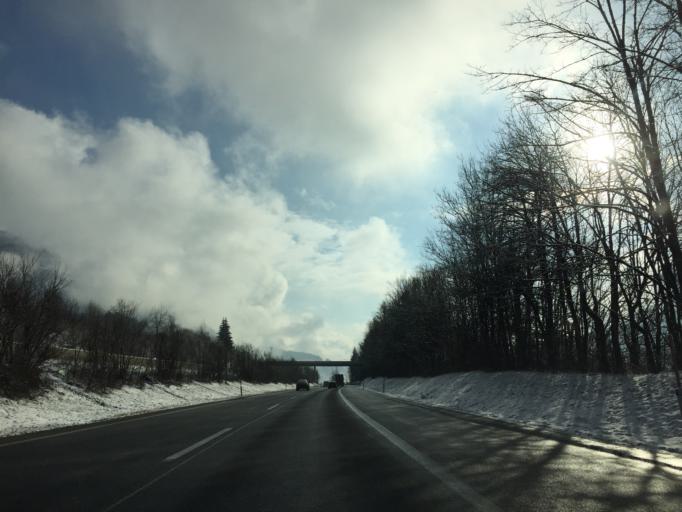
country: AT
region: Salzburg
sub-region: Politischer Bezirk Sankt Johann im Pongau
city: Werfenweng
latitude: 47.4352
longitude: 13.2501
